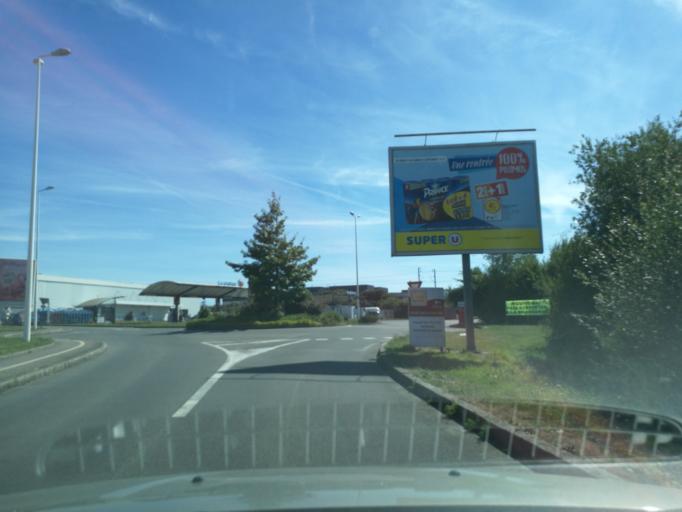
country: FR
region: Brittany
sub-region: Departement d'Ille-et-Vilaine
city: Montfort-sur-Meu
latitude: 48.1367
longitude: -1.9402
